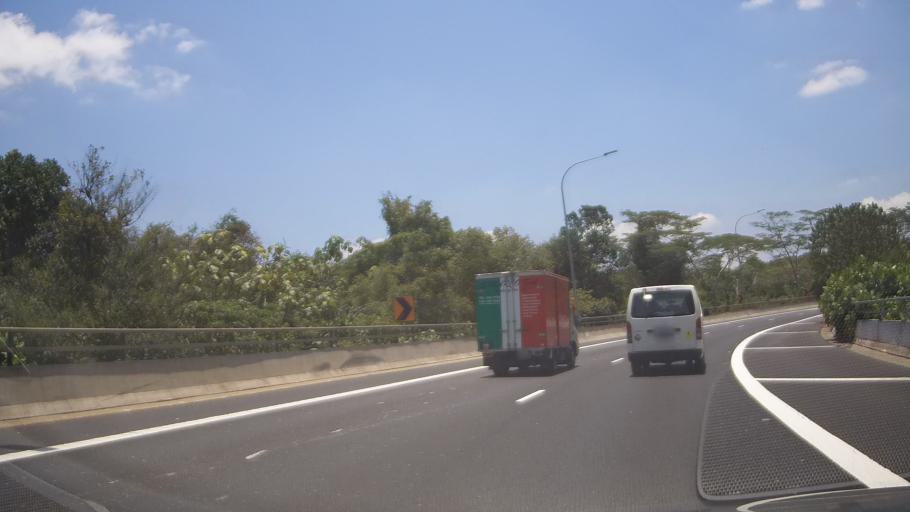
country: MY
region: Johor
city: Johor Bahru
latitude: 1.3927
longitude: 103.7759
